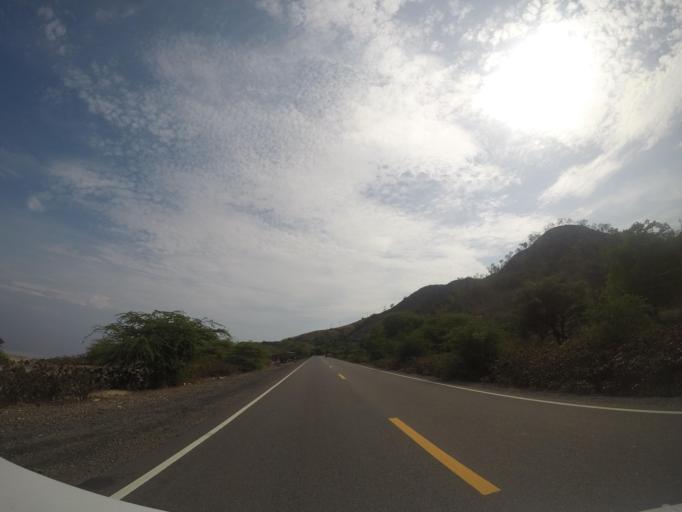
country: ID
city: Metinaro
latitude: -8.5248
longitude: 125.7120
